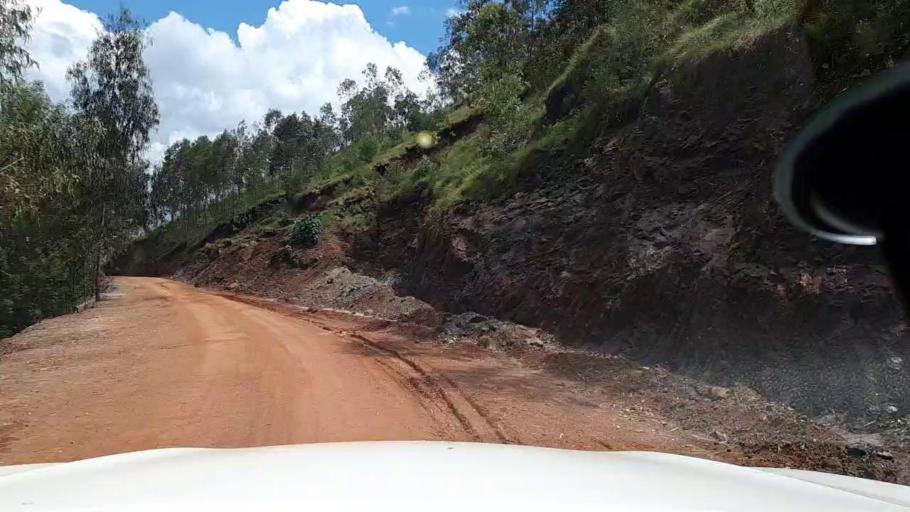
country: RW
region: Kigali
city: Kigali
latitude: -1.7843
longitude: 29.8431
